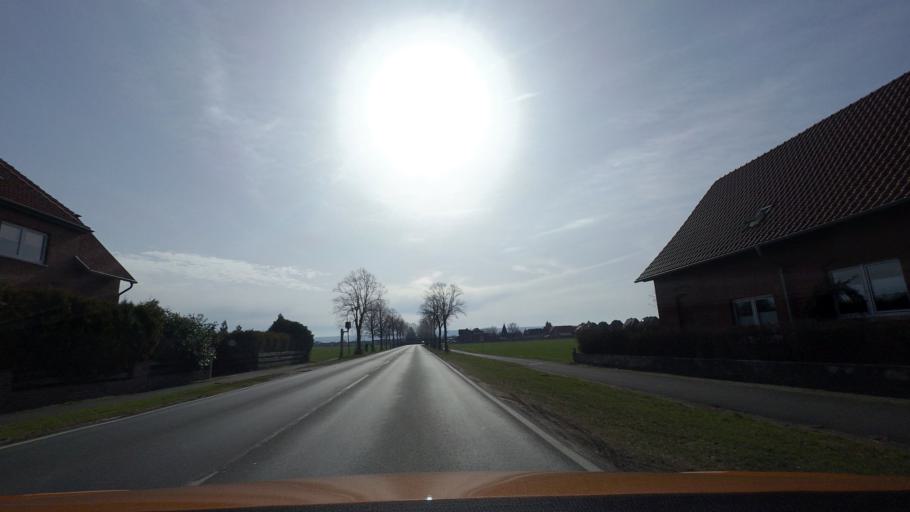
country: DE
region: Lower Saxony
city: Niedernwohren
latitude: 52.3611
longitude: 9.1387
